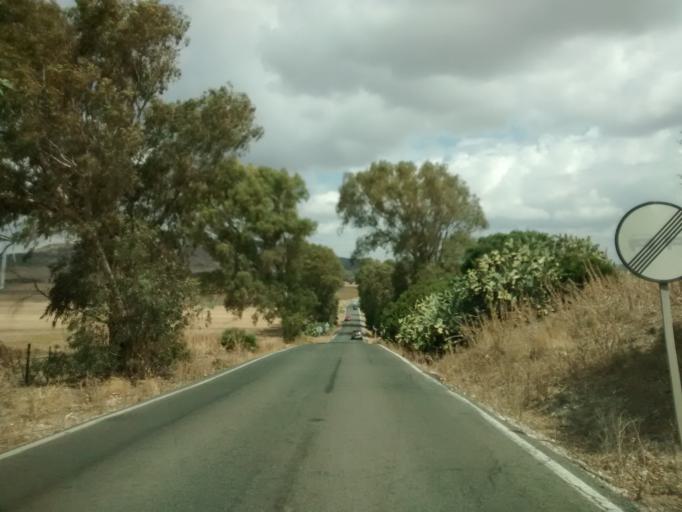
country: ES
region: Andalusia
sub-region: Provincia de Cadiz
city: Paterna de Rivera
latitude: 36.4995
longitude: -5.8858
